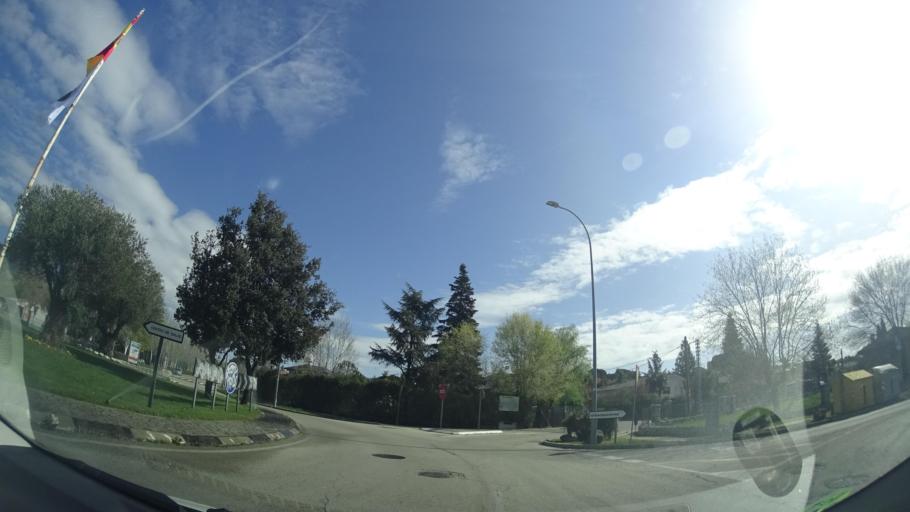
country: ES
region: Madrid
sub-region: Provincia de Madrid
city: Miraflores de la Sierra
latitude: 40.7492
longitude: -3.7829
